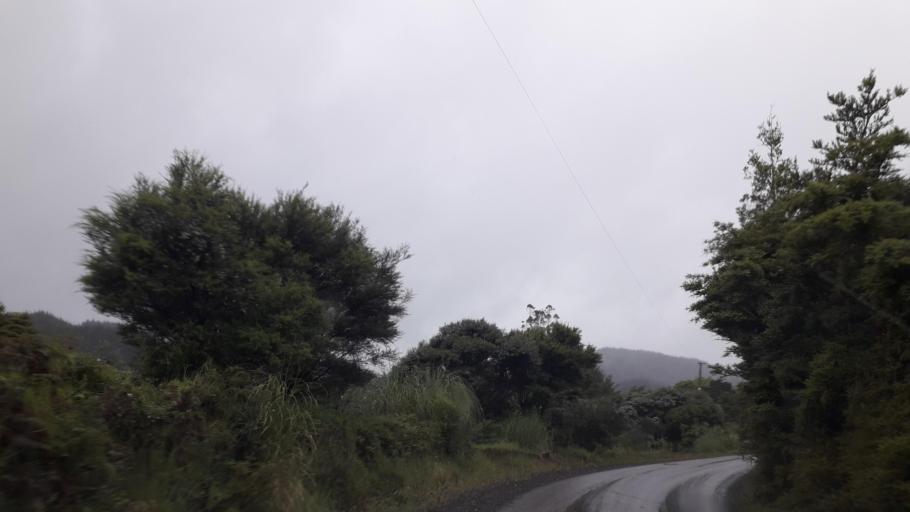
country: NZ
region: Northland
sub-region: Far North District
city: Kaitaia
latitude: -35.3807
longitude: 173.4097
